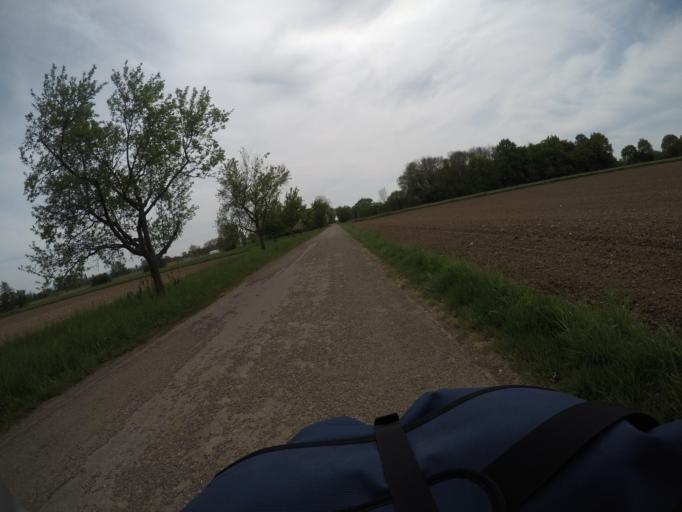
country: DE
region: Baden-Wuerttemberg
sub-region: Freiburg Region
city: Kehl
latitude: 48.5925
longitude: 7.8413
